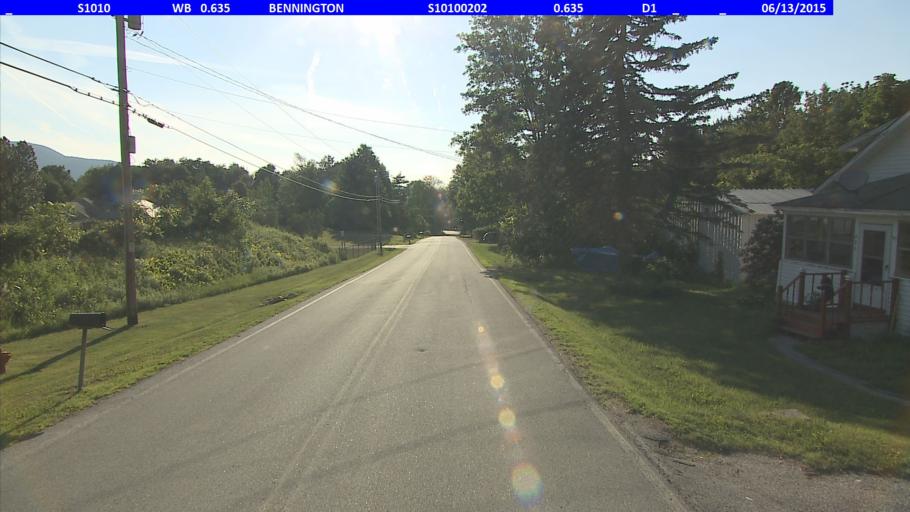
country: US
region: Vermont
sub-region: Bennington County
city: Bennington
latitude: 42.8780
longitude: -73.1634
